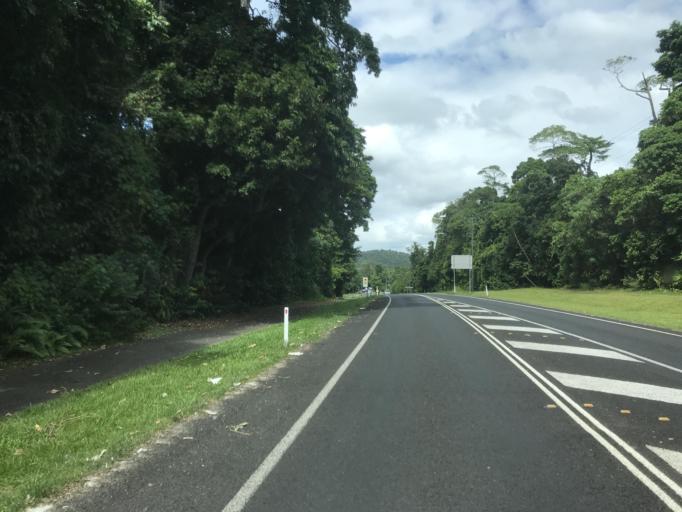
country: AU
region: Queensland
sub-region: Cassowary Coast
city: Innisfail
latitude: -17.8707
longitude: 146.0983
